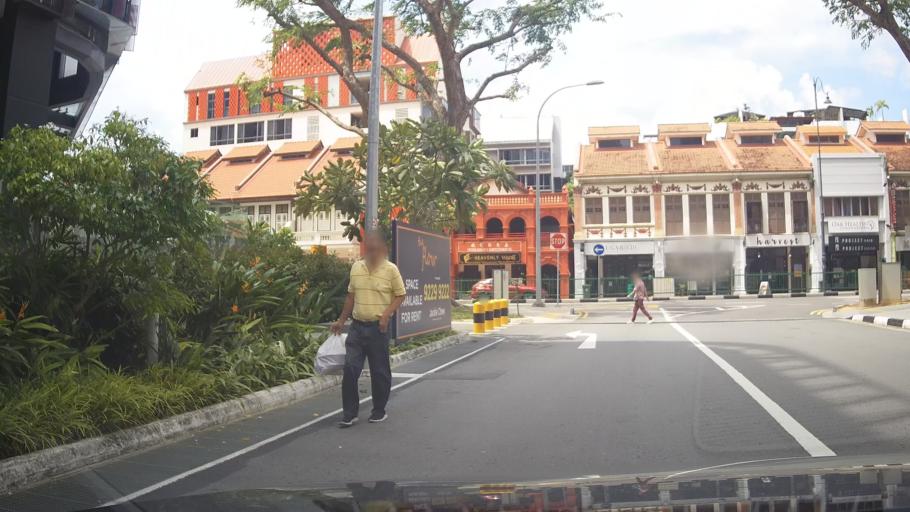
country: SG
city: Singapore
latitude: 1.3049
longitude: 103.9045
